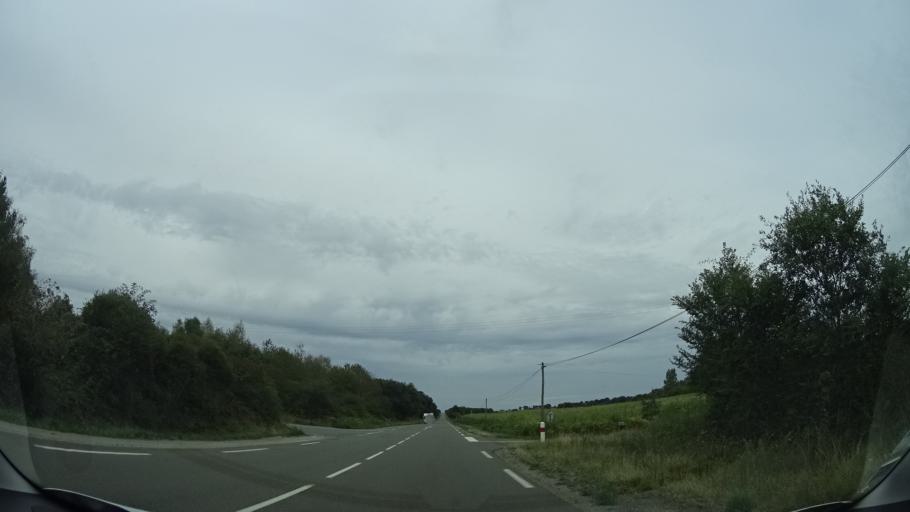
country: FR
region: Pays de la Loire
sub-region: Departement de la Mayenne
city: Meslay-du-Maine
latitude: 47.9867
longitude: -0.6206
